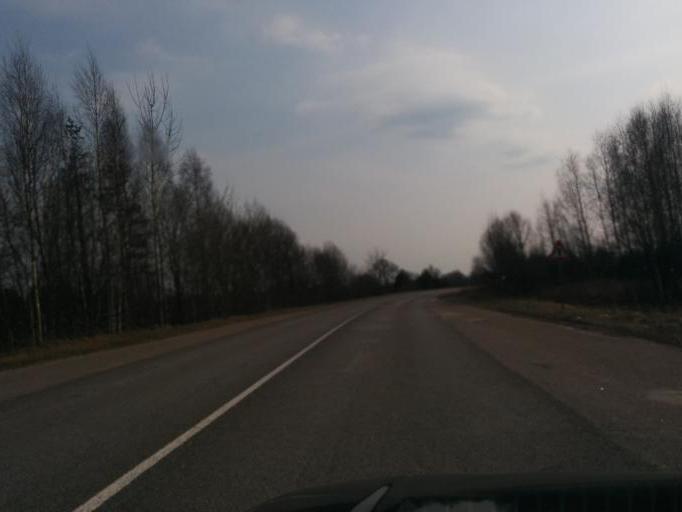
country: LV
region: Kekava
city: Balozi
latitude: 56.7764
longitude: 24.1107
